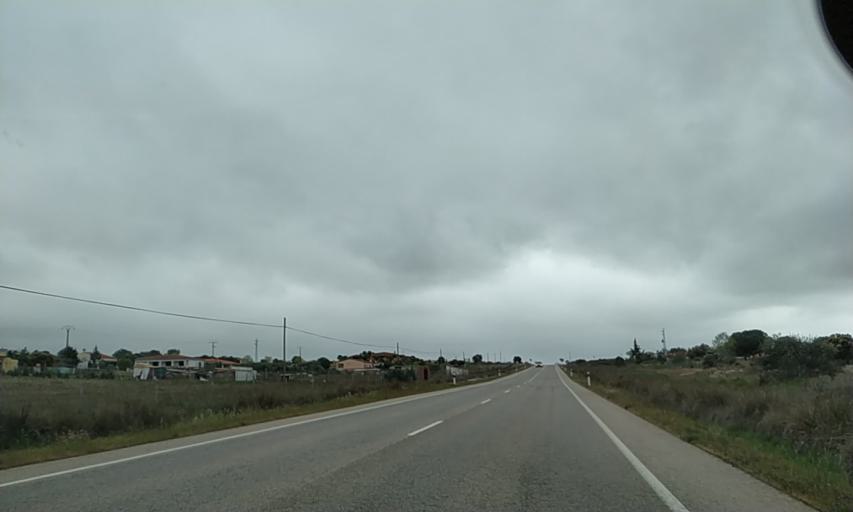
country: ES
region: Extremadura
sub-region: Provincia de Caceres
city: Malpartida de Caceres
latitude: 39.3844
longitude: -6.4408
